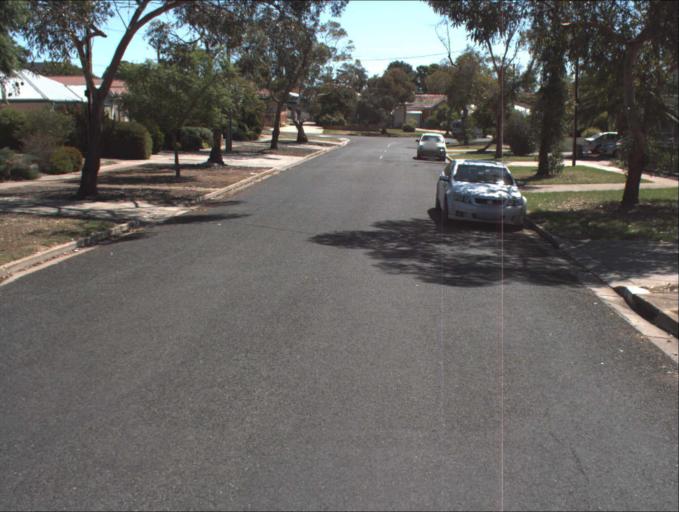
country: AU
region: South Australia
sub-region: Port Adelaide Enfield
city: Blair Athol
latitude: -34.8637
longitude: 138.6046
